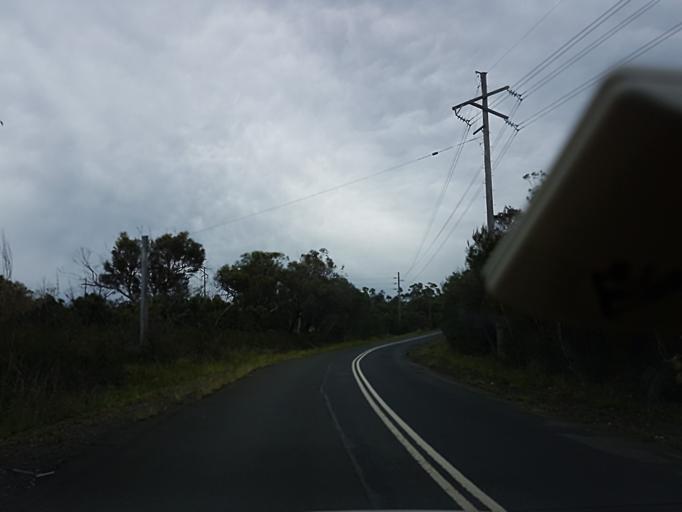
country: AU
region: New South Wales
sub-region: Warringah
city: Davidson
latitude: -33.7247
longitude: 151.2291
